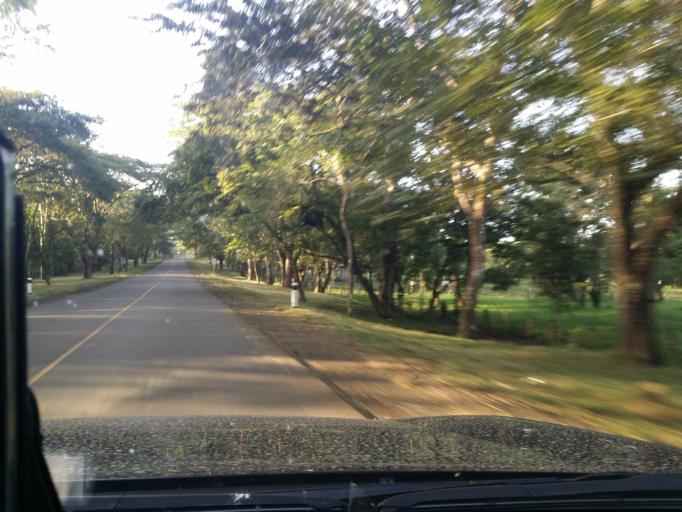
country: NI
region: Rio San Juan
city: San Miguelito
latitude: 11.4158
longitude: -84.8409
